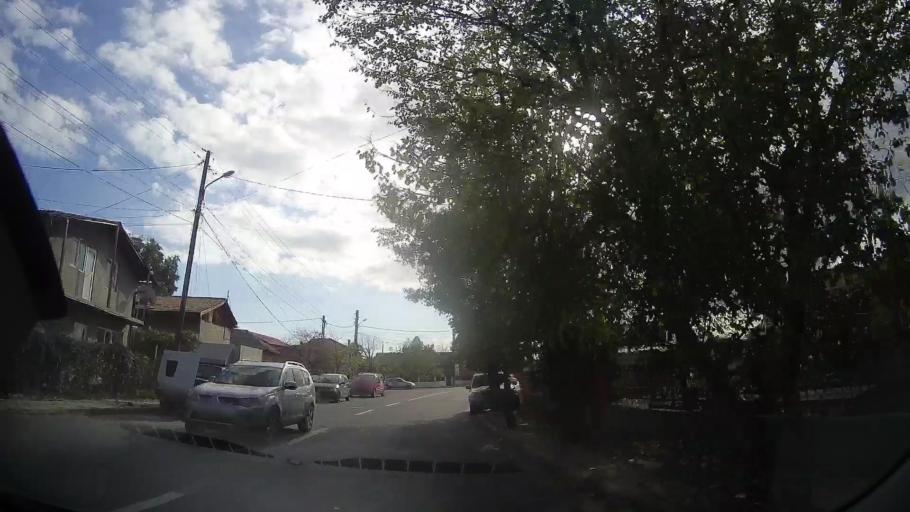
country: RO
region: Constanta
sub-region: Oras Techirghiol
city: Techirghiol
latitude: 44.0614
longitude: 28.5990
